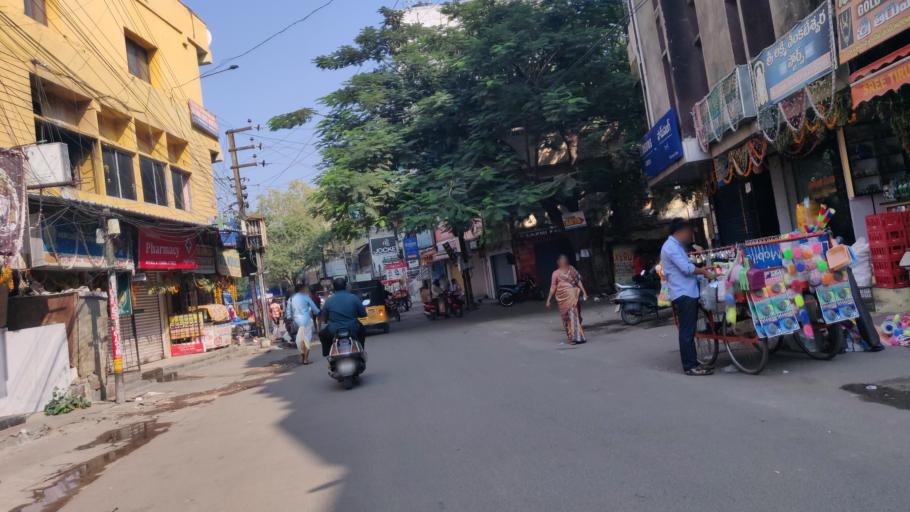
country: IN
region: Telangana
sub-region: Rangareddi
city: Gaddi Annaram
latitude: 17.3671
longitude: 78.5251
